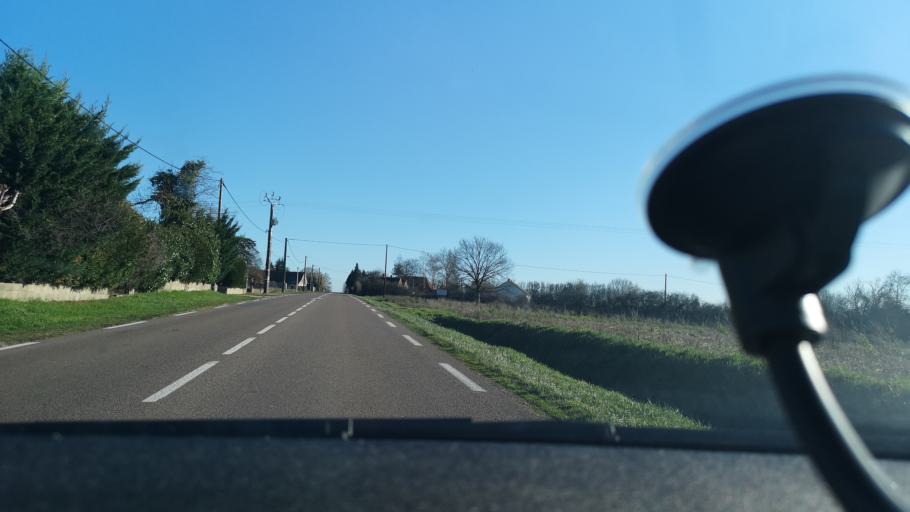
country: FR
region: Bourgogne
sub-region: Departement de Saone-et-Loire
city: Ouroux-sur-Saone
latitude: 46.7583
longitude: 4.9998
